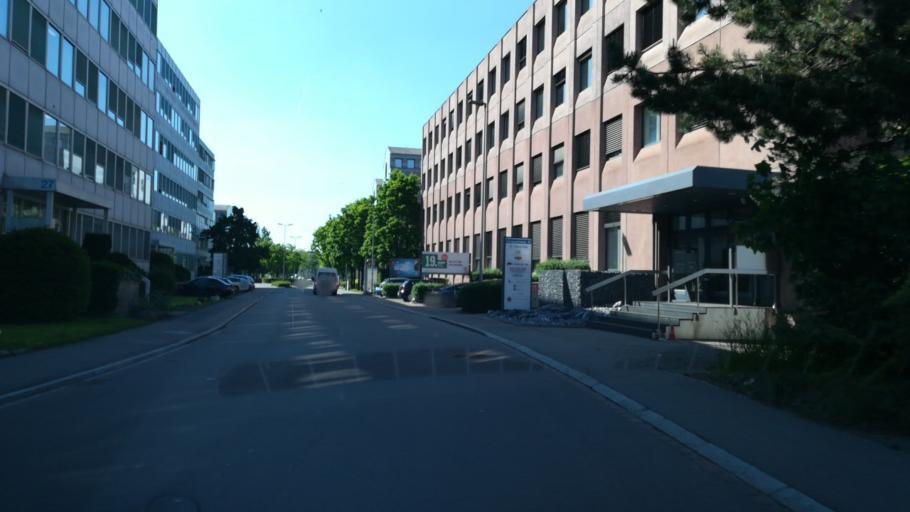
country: CH
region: Zurich
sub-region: Bezirk Buelach
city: Glattbrugg
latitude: 47.4344
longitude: 8.5617
